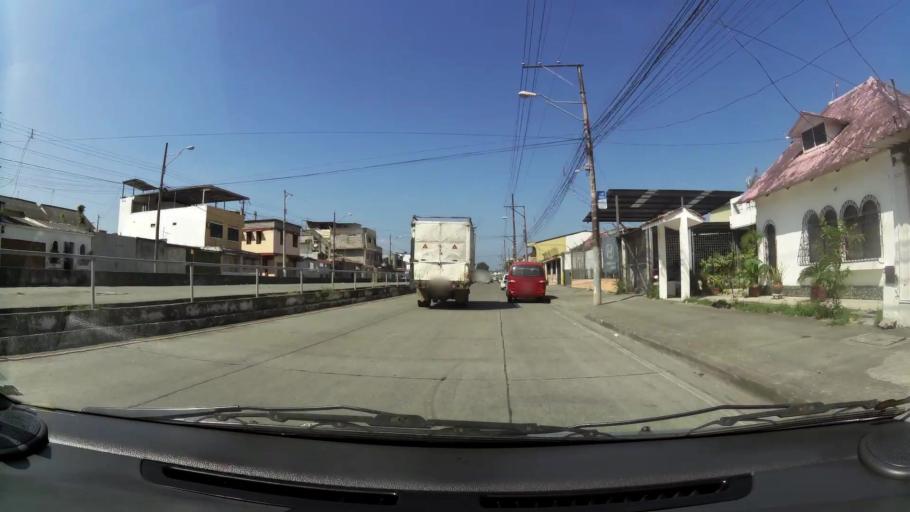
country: EC
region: Guayas
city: Eloy Alfaro
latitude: -2.1292
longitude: -79.9079
